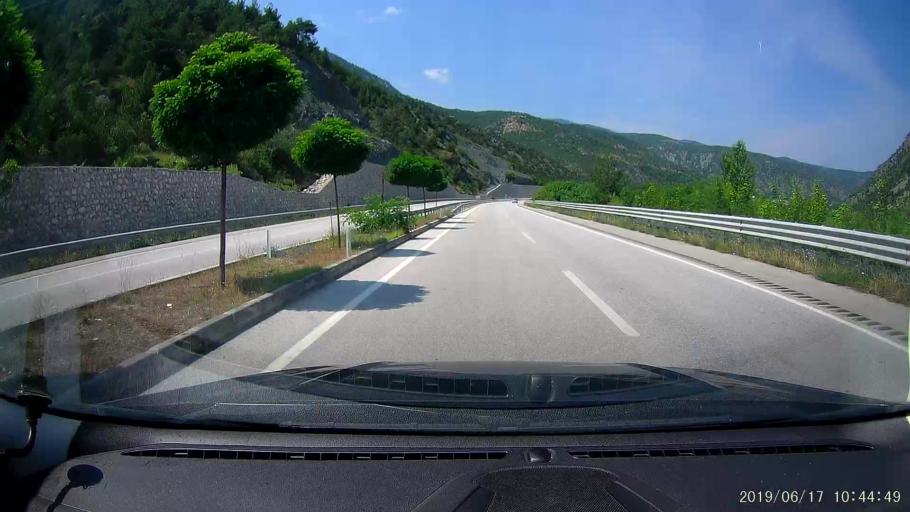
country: TR
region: Corum
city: Hacihamza
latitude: 41.0673
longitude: 34.5038
